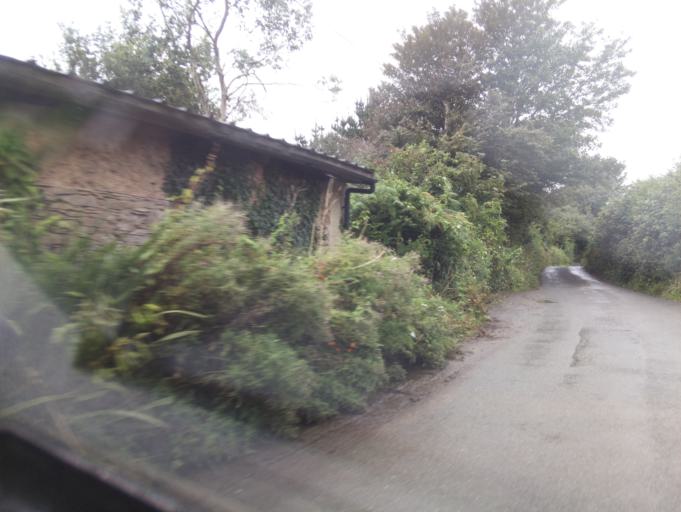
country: GB
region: England
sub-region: Devon
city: Dartmouth
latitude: 50.3467
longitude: -3.6391
